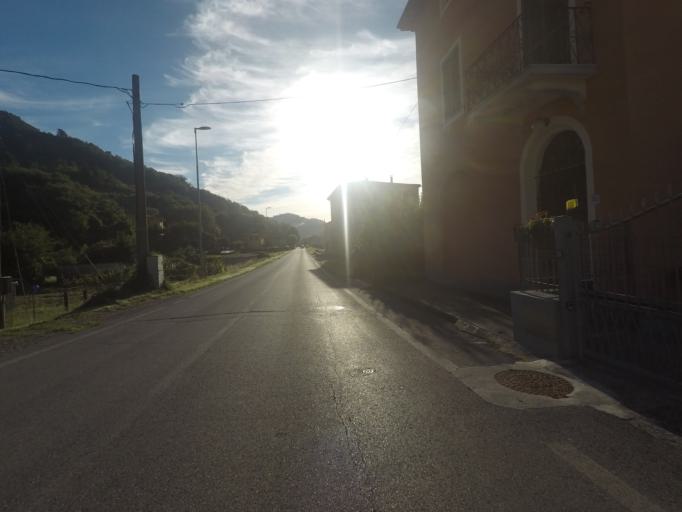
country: IT
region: Tuscany
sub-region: Provincia di Lucca
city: Pescaglia
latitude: 43.9522
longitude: 10.4347
